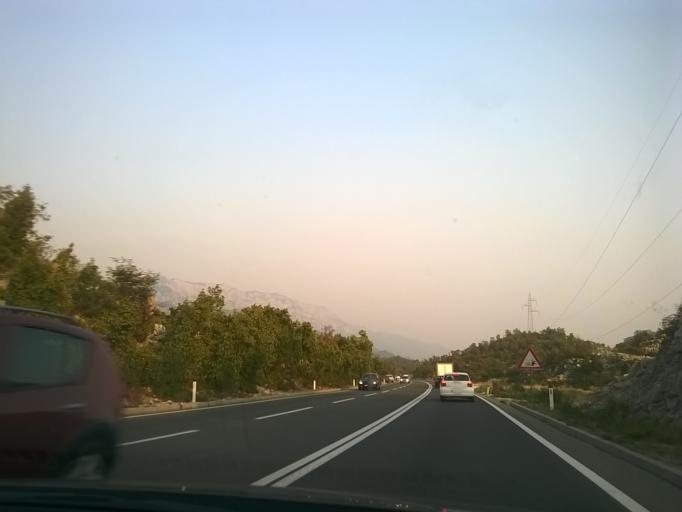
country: ME
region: Opstina Niksic
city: Niksic
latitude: 42.7097
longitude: 18.9537
